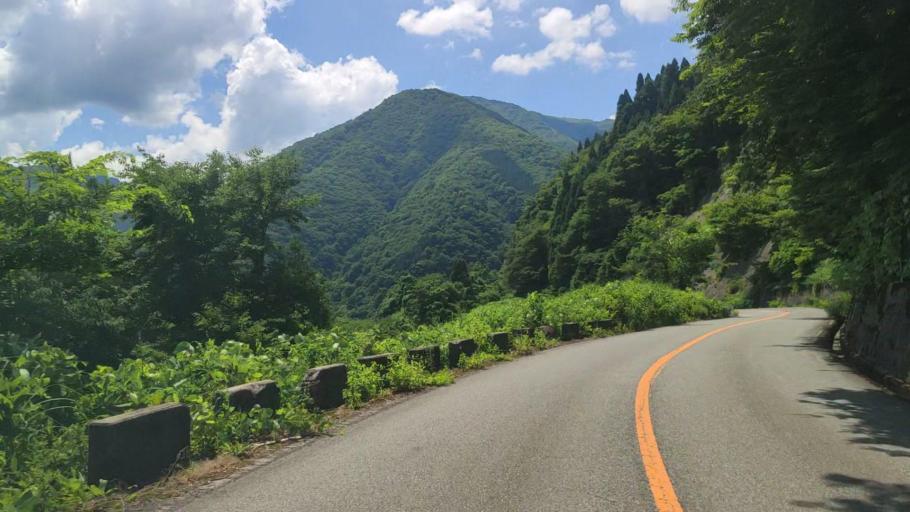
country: JP
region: Fukui
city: Ono
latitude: 35.9081
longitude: 136.5315
